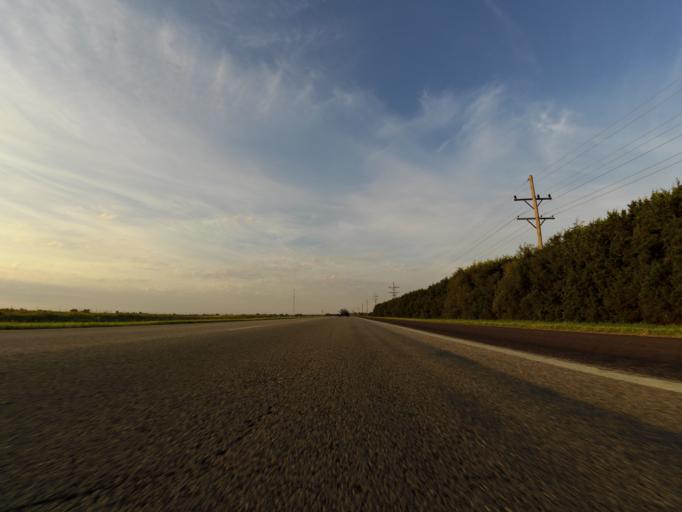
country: US
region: Kansas
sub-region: Reno County
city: South Hutchinson
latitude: 37.9818
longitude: -97.9406
